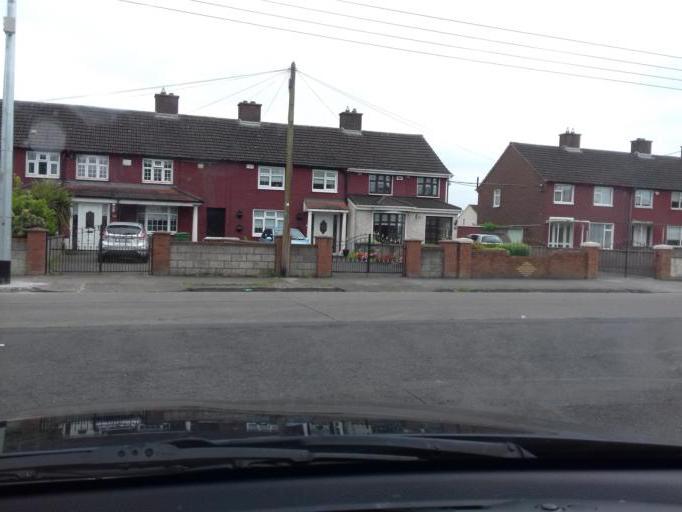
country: IE
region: Leinster
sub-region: Dublin City
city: Finglas
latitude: 53.3980
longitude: -6.3138
